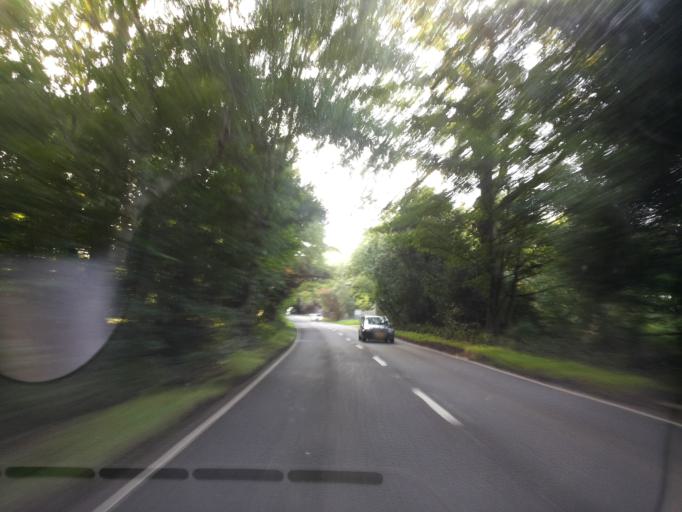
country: GB
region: England
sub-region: Surrey
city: Ottershaw
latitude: 51.3799
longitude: -0.5434
